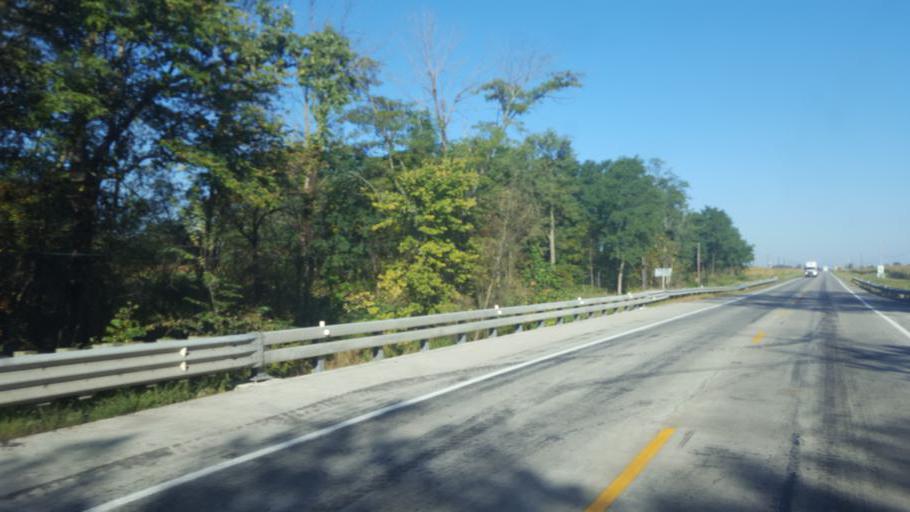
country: US
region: Ohio
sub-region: Hardin County
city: Kenton
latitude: 40.5040
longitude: -83.4970
